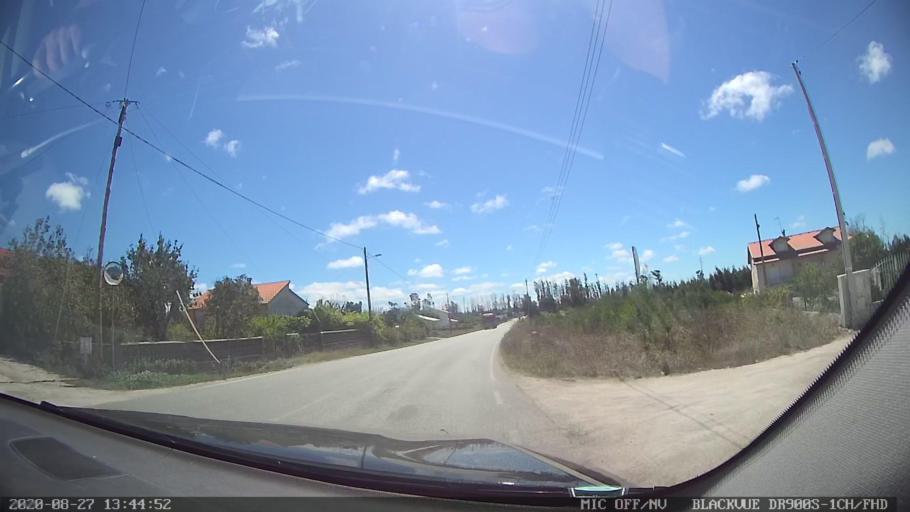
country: PT
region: Coimbra
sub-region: Mira
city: Mira
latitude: 40.4106
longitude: -8.7344
